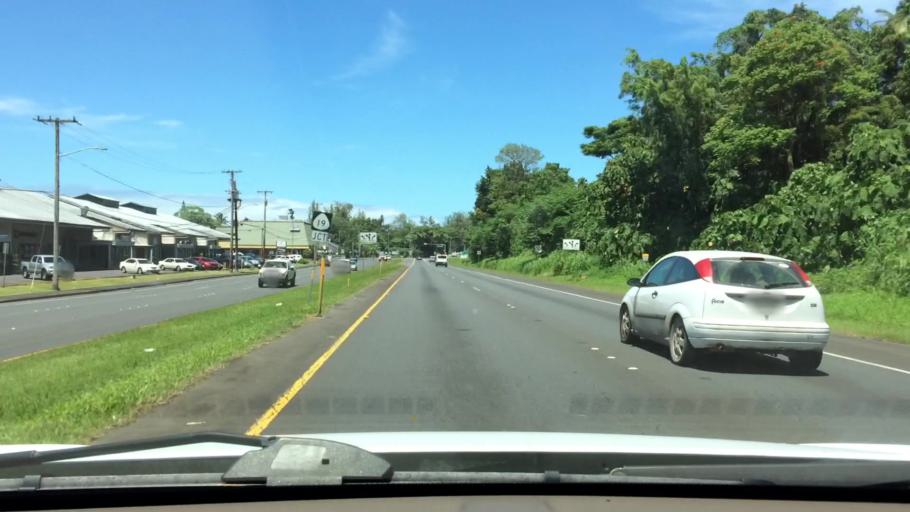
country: US
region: Hawaii
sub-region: Hawaii County
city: Hilo
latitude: 19.7194
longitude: -155.0638
